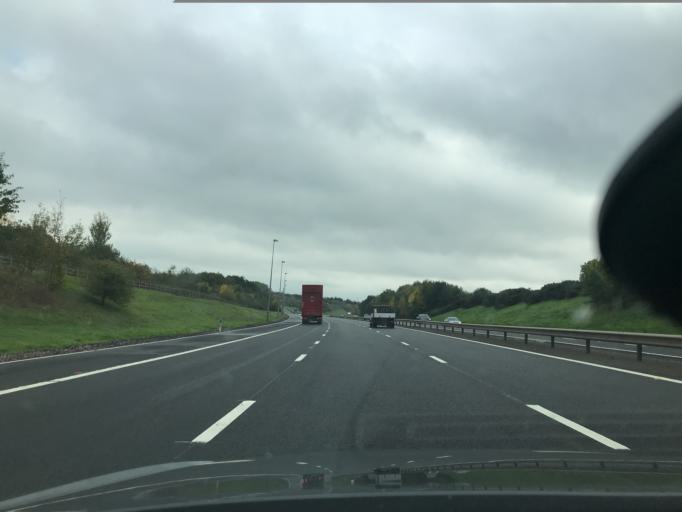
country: GB
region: England
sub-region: City and Borough of Birmingham
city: Sutton Coldfield
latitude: 52.5822
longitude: -1.7869
